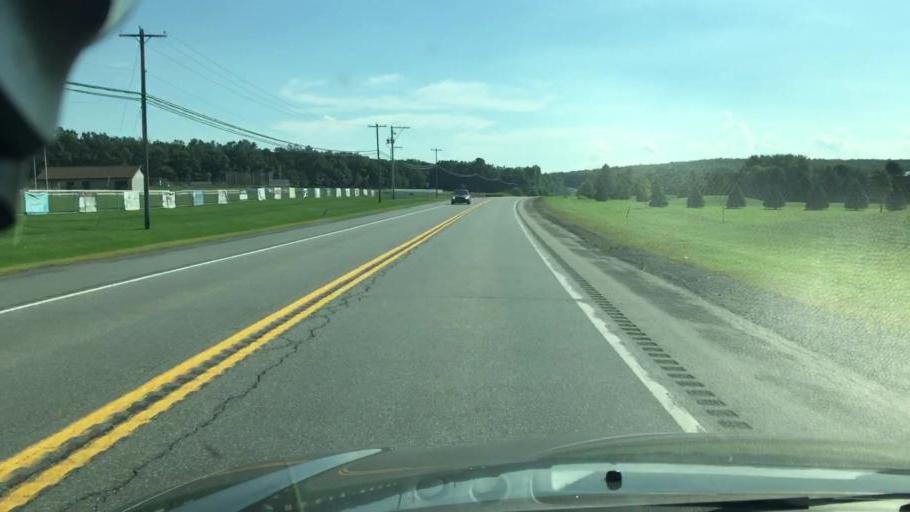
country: US
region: Pennsylvania
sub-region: Carbon County
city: Jim Thorpe
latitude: 40.9328
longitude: -75.6584
